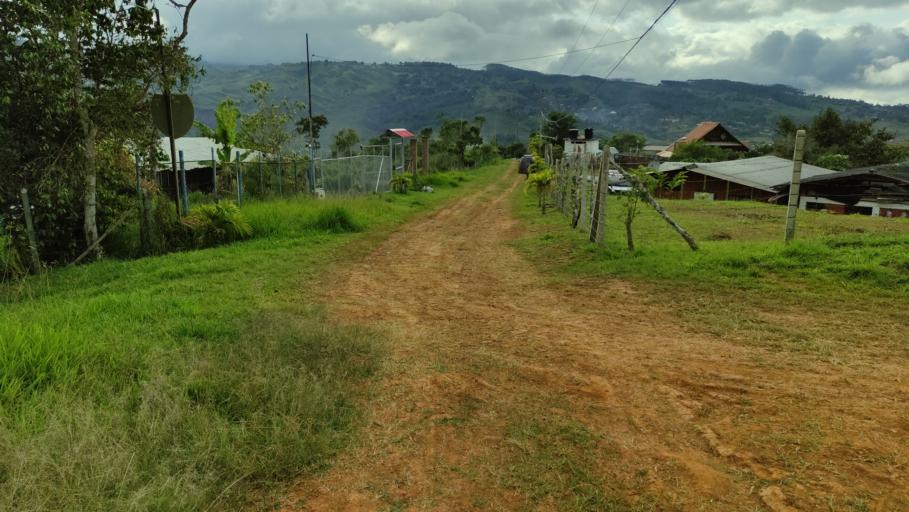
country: CO
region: Valle del Cauca
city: Dagua
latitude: 3.5370
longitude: -76.6397
